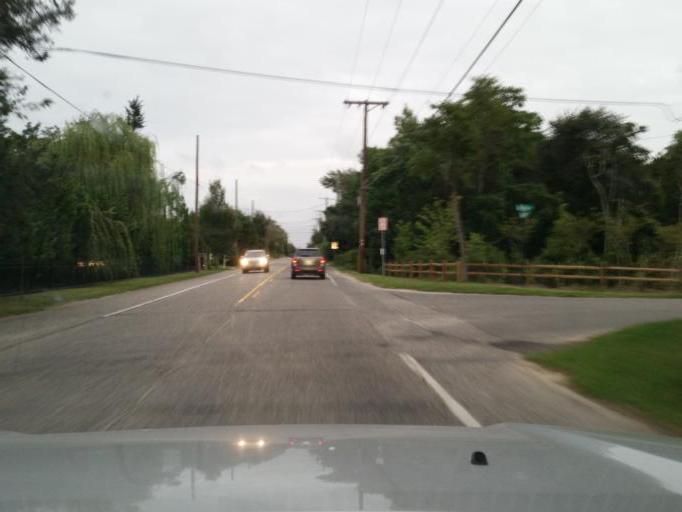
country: US
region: New Jersey
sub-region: Cape May County
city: West Cape May
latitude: 38.9402
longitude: -74.9522
